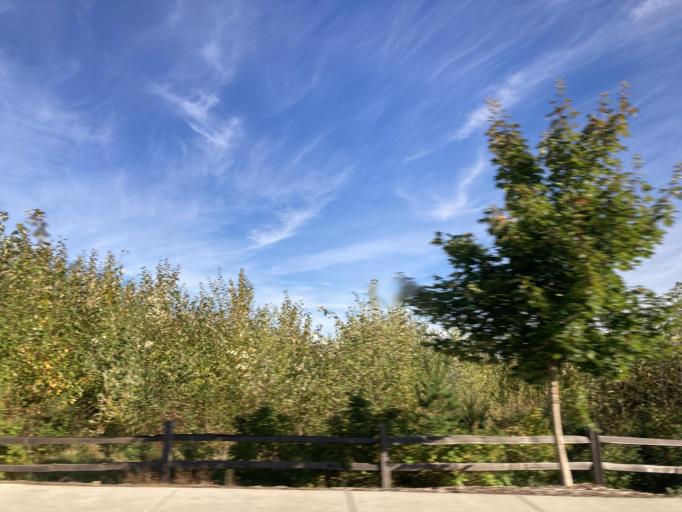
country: US
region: Washington
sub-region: Whatcom County
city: Marietta-Alderwood
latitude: 48.8151
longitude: -122.5051
